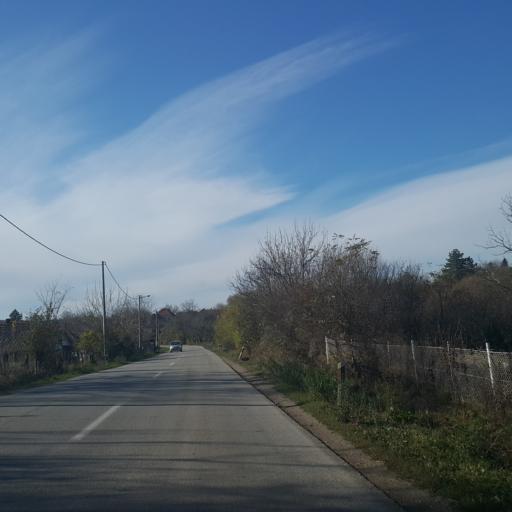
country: RS
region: Central Serbia
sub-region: Sumadijski Okrug
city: Topola
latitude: 44.2486
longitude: 20.7319
